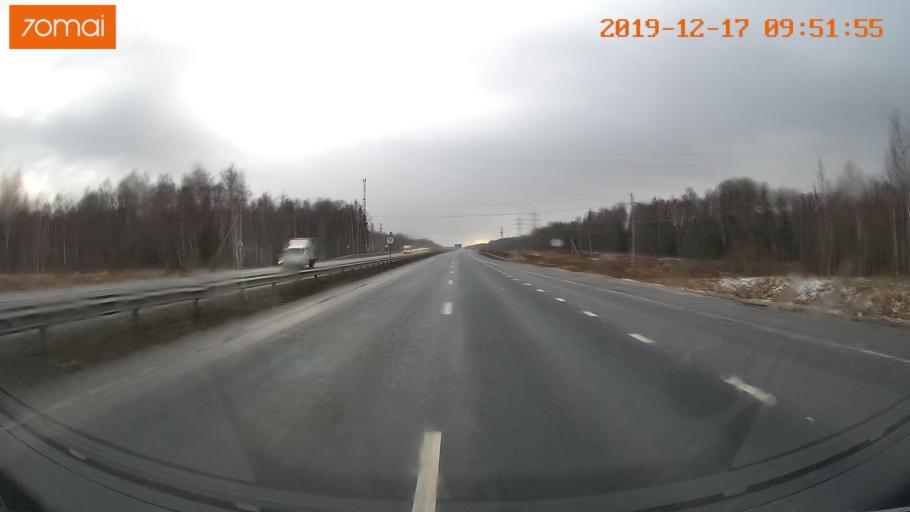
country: RU
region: Vladimir
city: Kommunar
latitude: 56.0385
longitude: 40.5288
